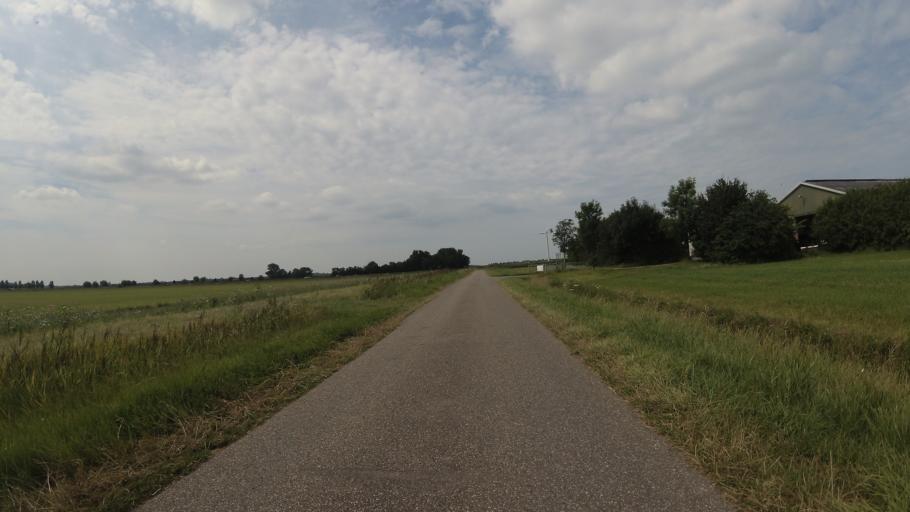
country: NL
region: Zeeland
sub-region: Gemeente Noord-Beveland
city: Kamperland
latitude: 51.5854
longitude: 3.6953
